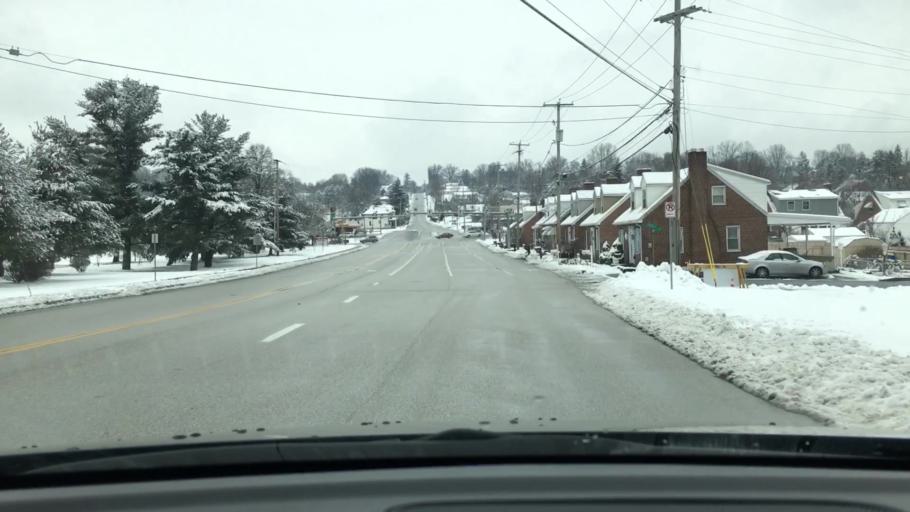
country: US
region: Pennsylvania
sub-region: York County
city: East York
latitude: 39.9805
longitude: -76.7089
